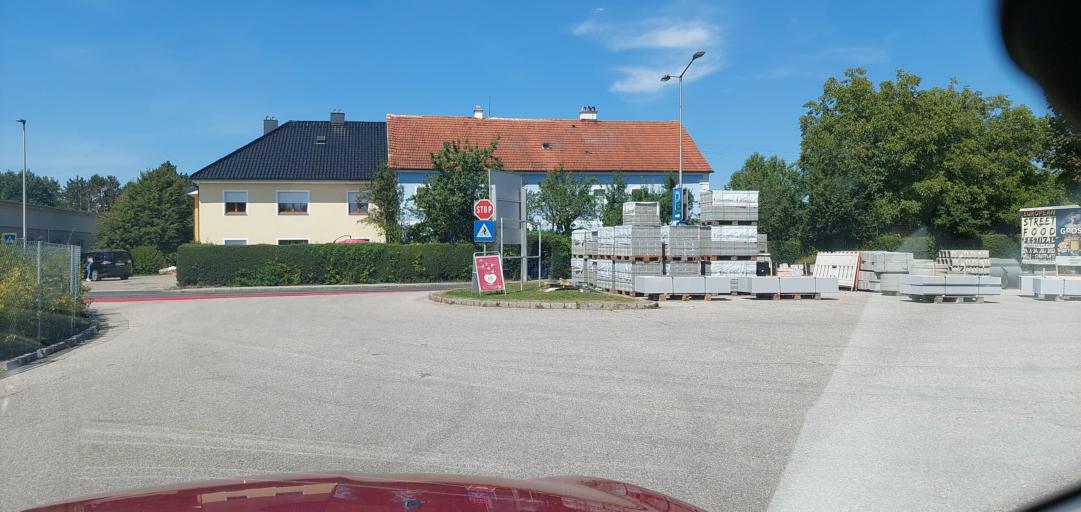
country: AT
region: Upper Austria
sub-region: Wels-Land
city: Stadl-Paura
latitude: 48.0903
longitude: 13.8652
